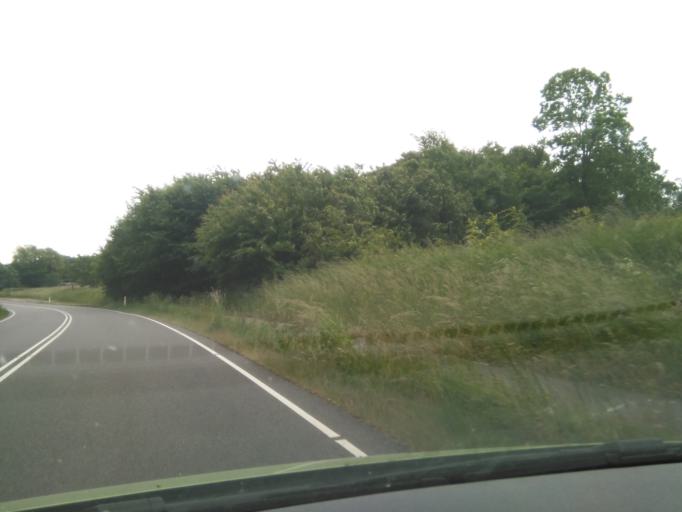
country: DK
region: Capital Region
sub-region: Bornholm Kommune
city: Akirkeby
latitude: 55.2349
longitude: 14.8746
